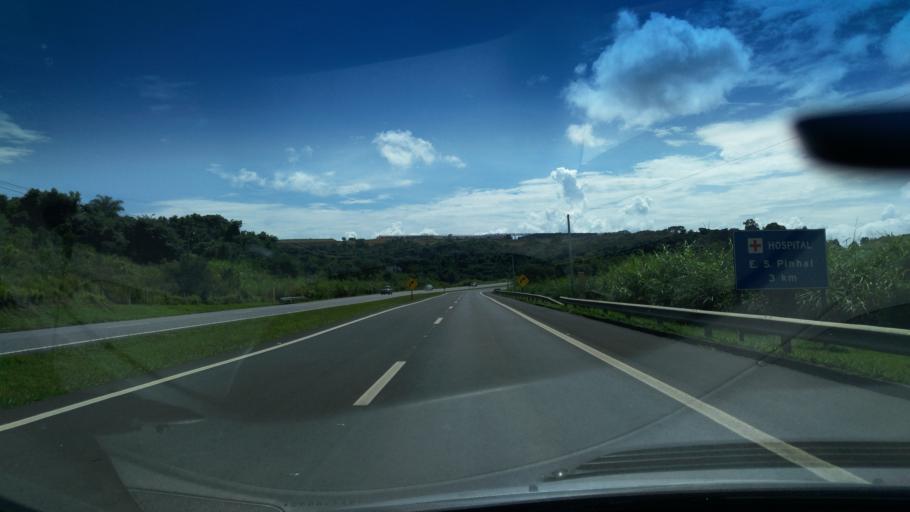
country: BR
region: Sao Paulo
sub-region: Santo Antonio Do Jardim
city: Espirito Santo do Pinhal
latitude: -22.2139
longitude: -46.7852
